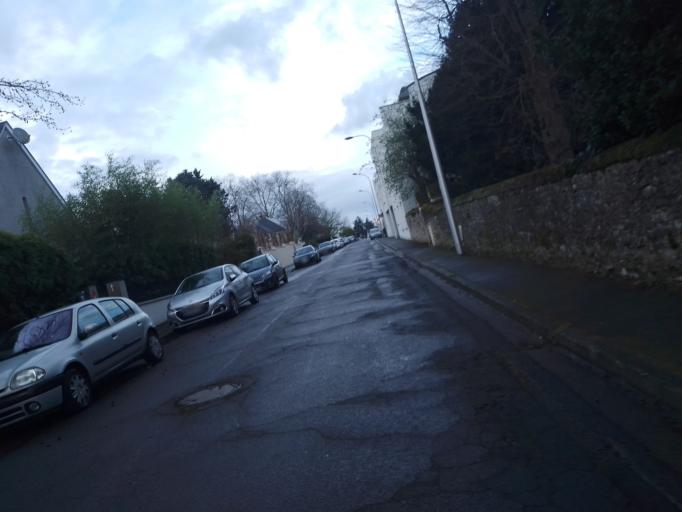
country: FR
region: Centre
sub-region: Departement du Loir-et-Cher
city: Blois
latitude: 47.5968
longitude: 1.3468
